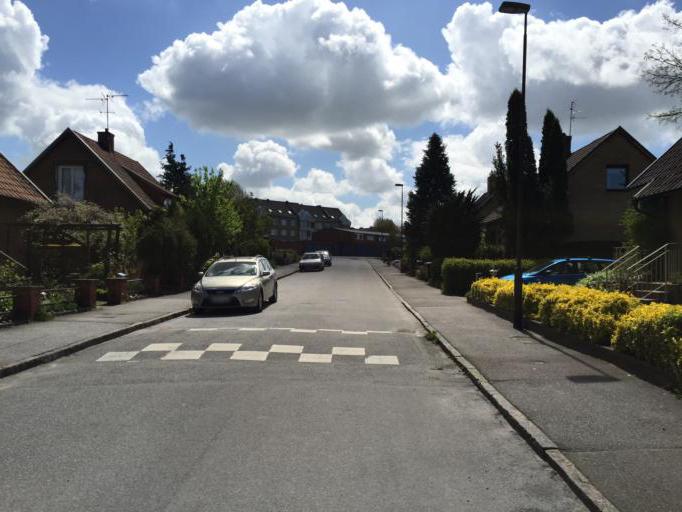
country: SE
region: Skane
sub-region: Lunds Kommun
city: Lund
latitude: 55.7178
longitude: 13.1716
